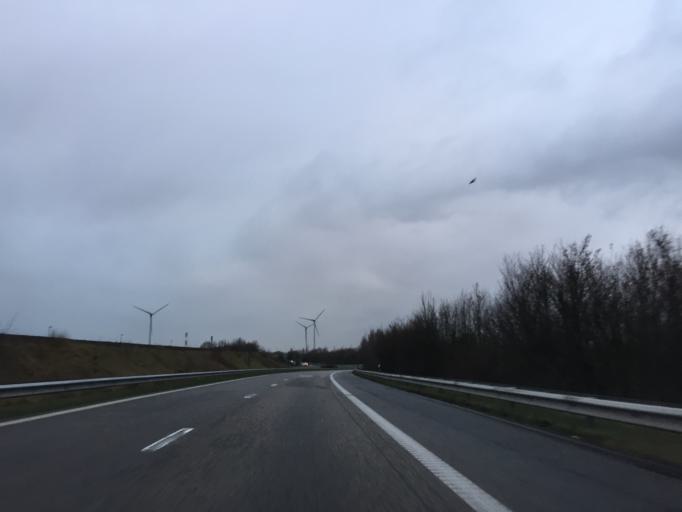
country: NL
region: North Brabant
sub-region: Gemeente Woensdrecht
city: Woensdrecht
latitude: 51.3663
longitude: 4.3164
